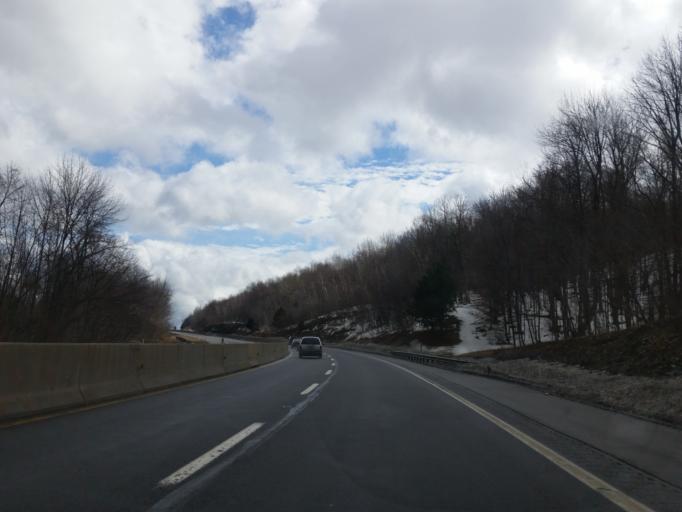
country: US
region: Pennsylvania
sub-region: Lackawanna County
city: Clarks Summit
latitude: 41.4682
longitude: -75.7029
